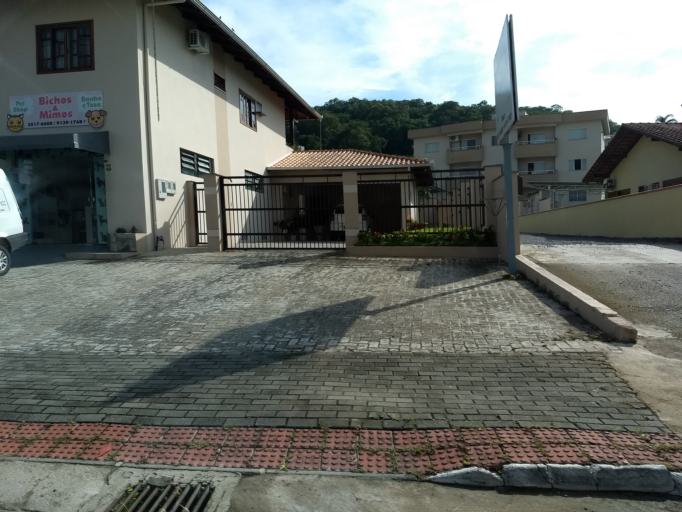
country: BR
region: Santa Catarina
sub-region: Jaragua Do Sul
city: Jaragua do Sul
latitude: -26.4683
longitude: -49.0979
